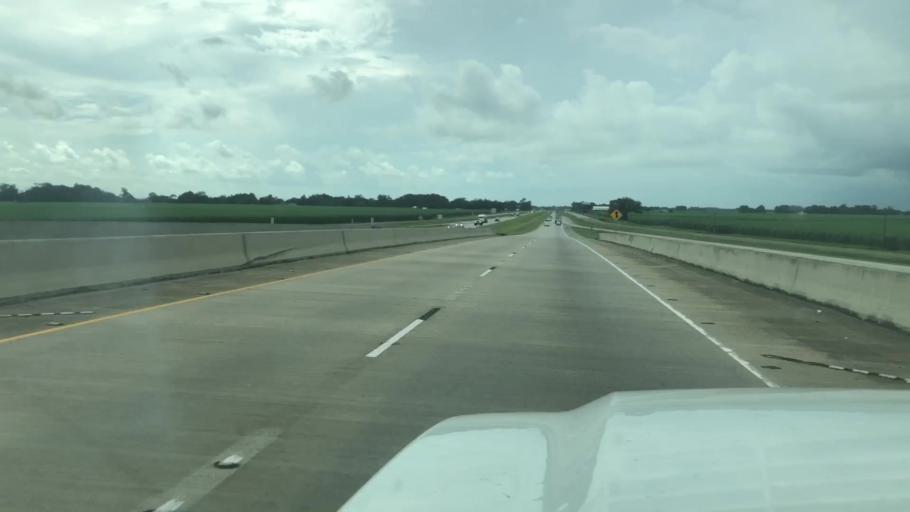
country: US
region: Louisiana
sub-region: Iberia Parish
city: Jeanerette
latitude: 29.9205
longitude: -91.7296
